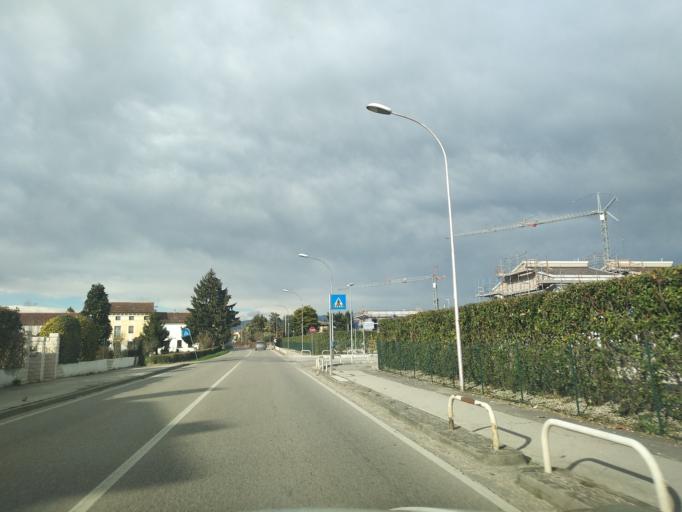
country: IT
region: Veneto
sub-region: Provincia di Vicenza
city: Bolzano Vicentino
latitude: 45.6064
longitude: 11.6231
